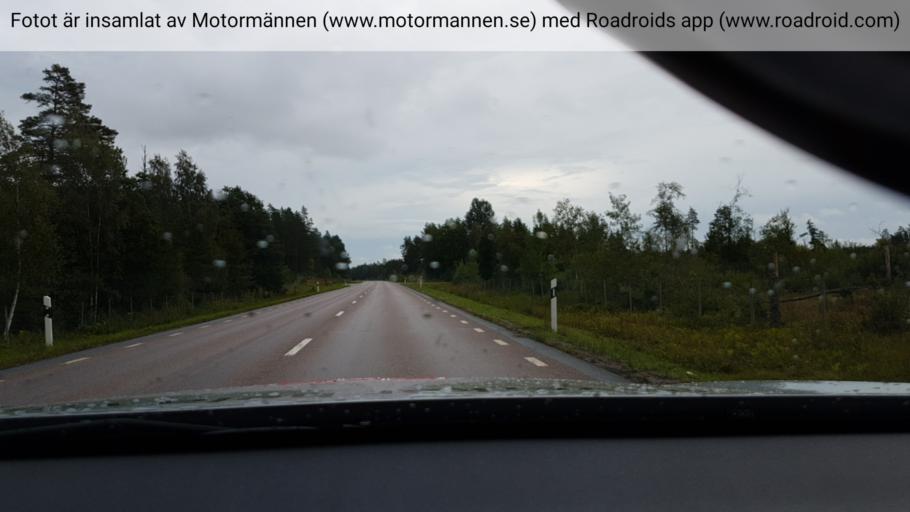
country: SE
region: Uppsala
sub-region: Tierps Kommun
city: Karlholmsbruk
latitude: 60.4338
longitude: 17.8030
